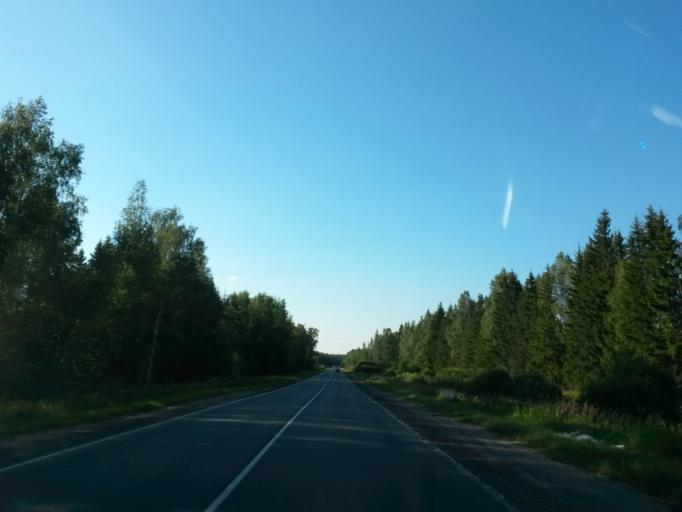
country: RU
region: Ivanovo
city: Pistsovo
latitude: 57.0923
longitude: 40.6626
